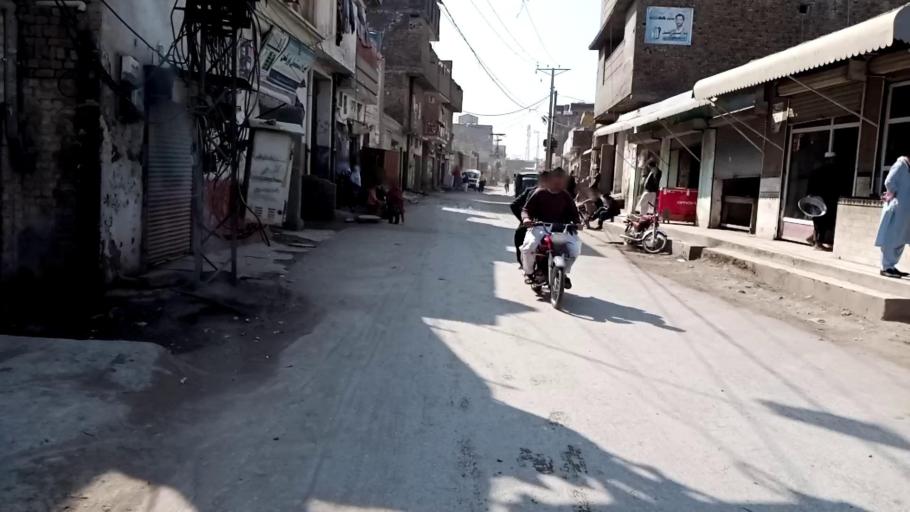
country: PK
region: Khyber Pakhtunkhwa
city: Peshawar
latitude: 34.0117
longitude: 71.5117
